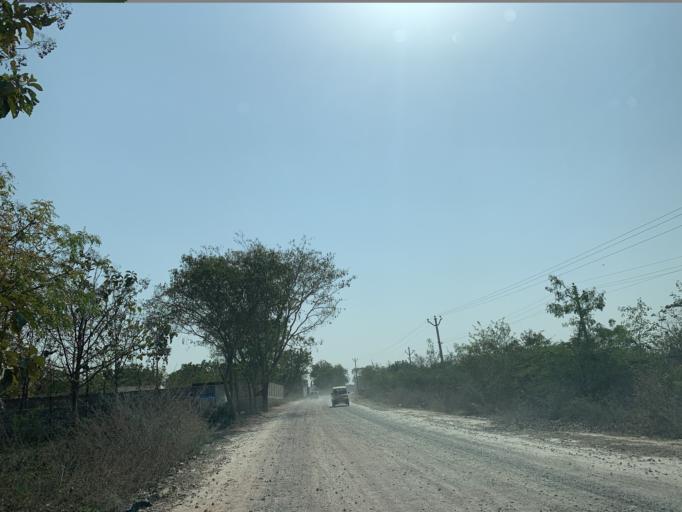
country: IN
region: Telangana
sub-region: Rangareddi
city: Sriramnagar
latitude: 17.3287
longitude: 78.2959
